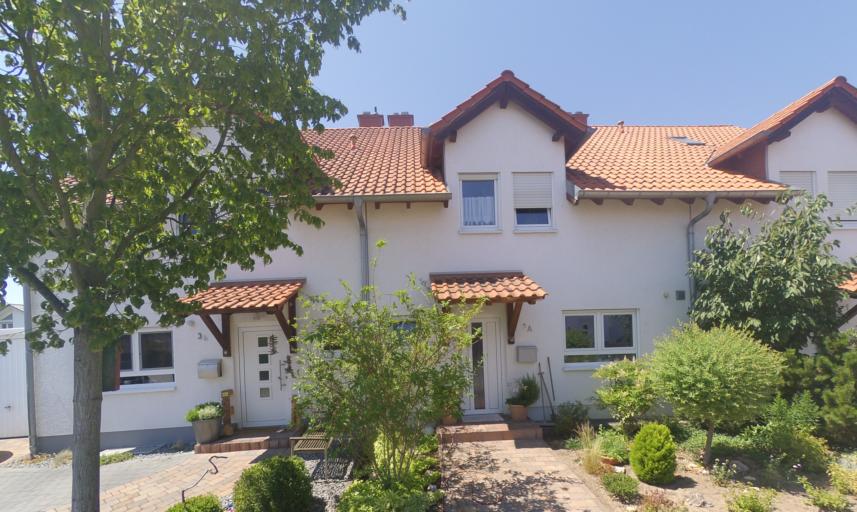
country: DE
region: Rheinland-Pfalz
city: Limburgerhof
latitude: 49.4255
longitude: 8.4013
